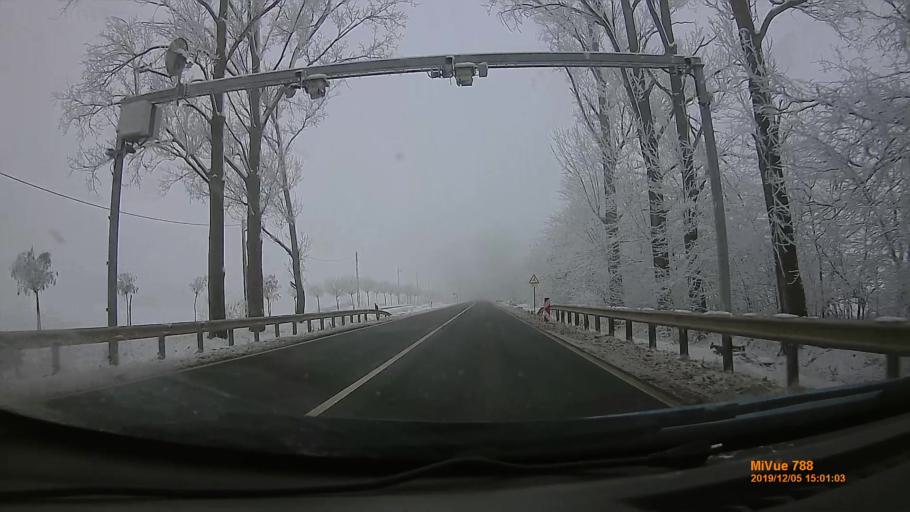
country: HU
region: Szabolcs-Szatmar-Bereg
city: Tiszanagyfalu
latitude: 48.0665
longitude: 21.5323
